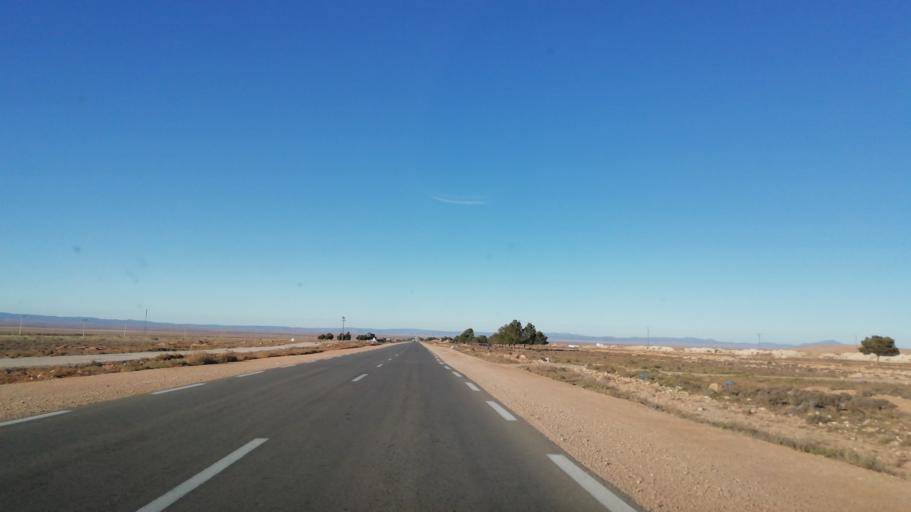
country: DZ
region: Tlemcen
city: Sebdou
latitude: 34.3039
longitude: -1.2616
